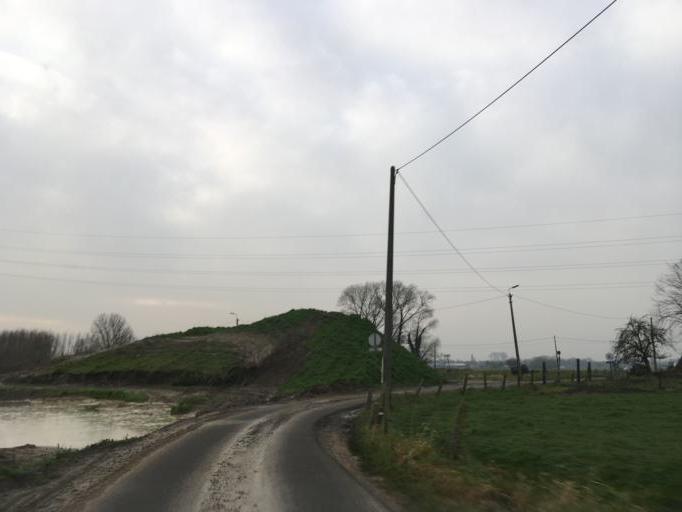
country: BE
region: Flanders
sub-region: Provincie West-Vlaanderen
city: Waregem
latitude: 50.8595
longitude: 3.4438
